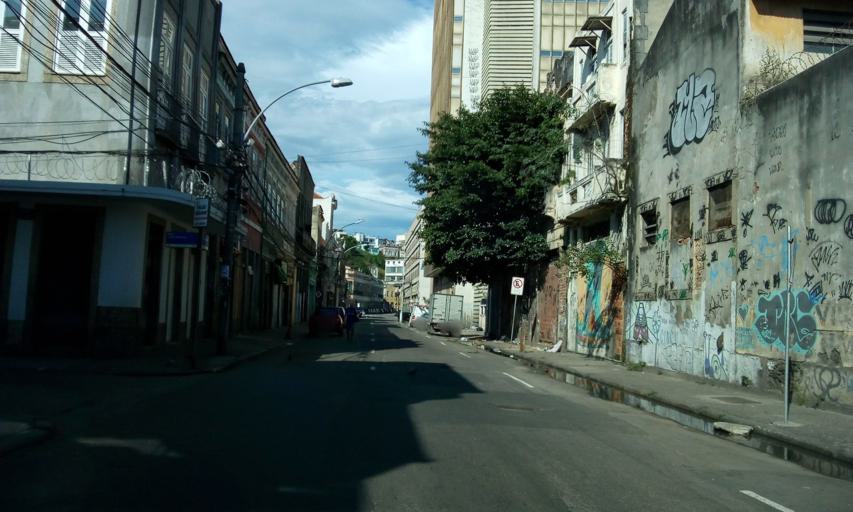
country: BR
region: Rio de Janeiro
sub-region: Rio De Janeiro
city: Rio de Janeiro
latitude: -22.9009
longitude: -43.1889
